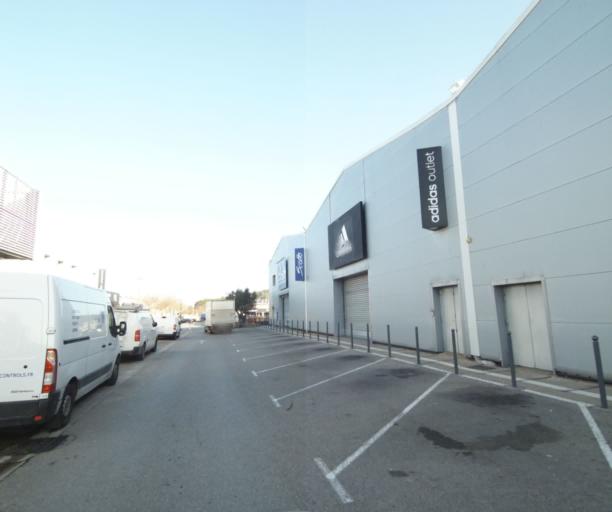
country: FR
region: Provence-Alpes-Cote d'Azur
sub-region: Departement des Bouches-du-Rhone
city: Septemes-les-Vallons
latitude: 43.4187
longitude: 5.3583
